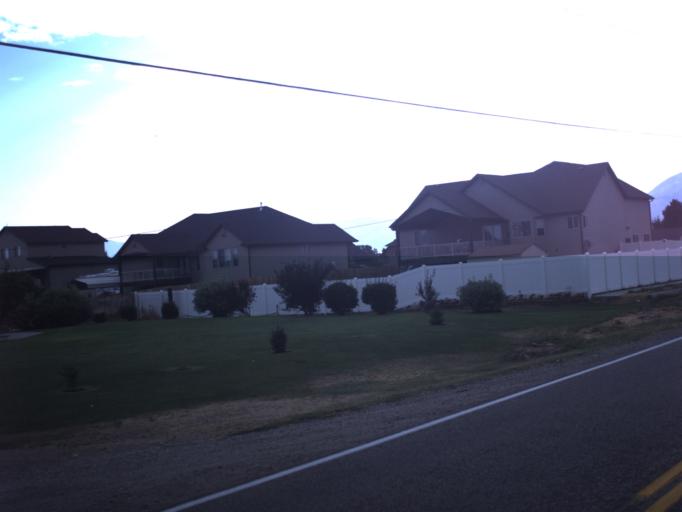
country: US
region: Utah
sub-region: Weber County
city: Hooper
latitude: 41.1639
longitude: -112.0999
